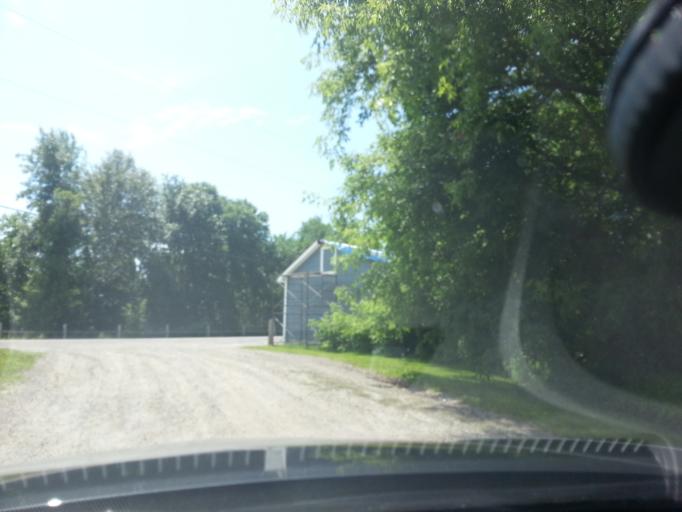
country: CA
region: Ontario
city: Renfrew
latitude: 45.2988
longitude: -76.7261
